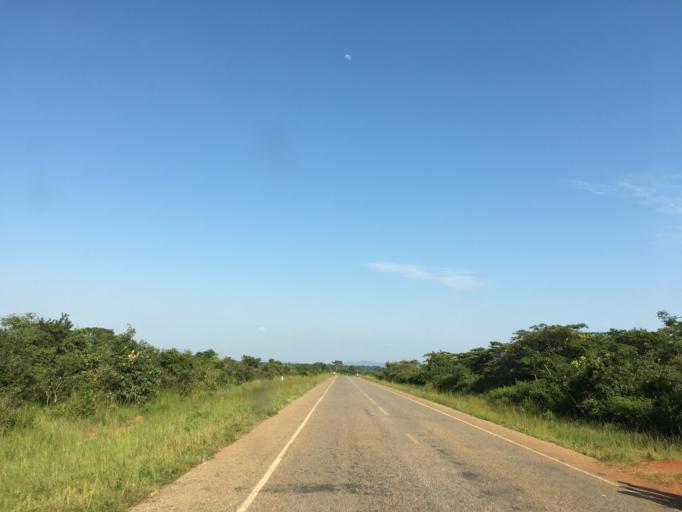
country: UG
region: Western Region
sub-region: Kiryandongo District
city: Masindi Port
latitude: 1.5766
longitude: 31.9376
